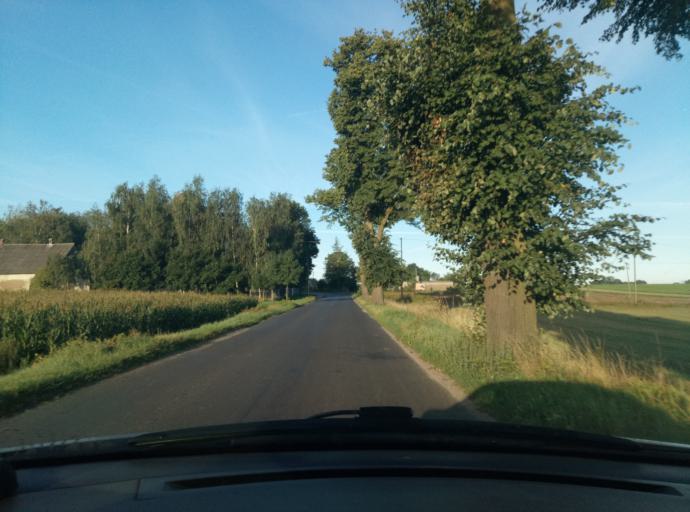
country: PL
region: Kujawsko-Pomorskie
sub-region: Powiat brodnicki
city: Jablonowo Pomorskie
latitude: 53.3987
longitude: 19.1620
